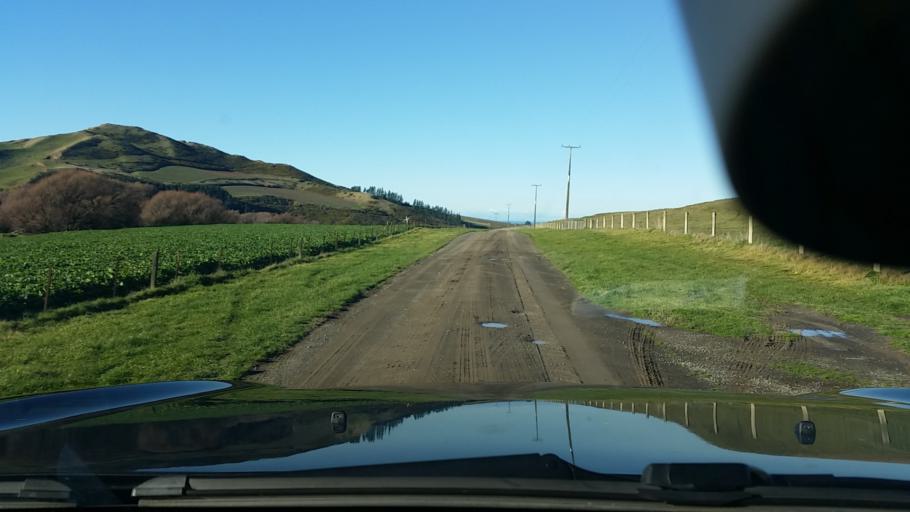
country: NZ
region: Marlborough
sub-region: Marlborough District
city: Blenheim
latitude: -41.6386
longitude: 174.0243
